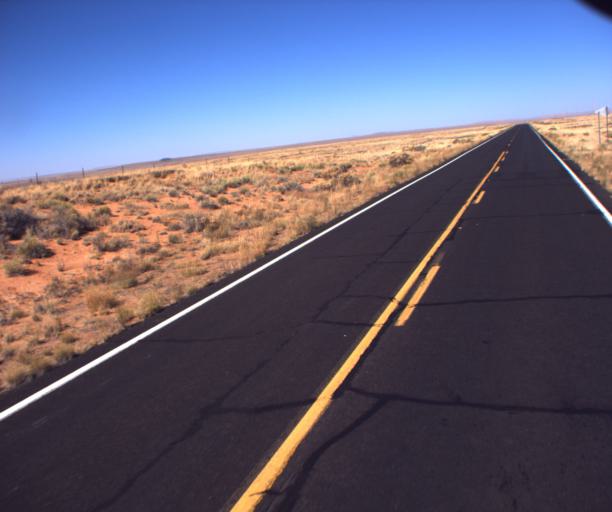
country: US
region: Arizona
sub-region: Navajo County
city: Dilkon
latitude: 35.5327
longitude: -110.4463
